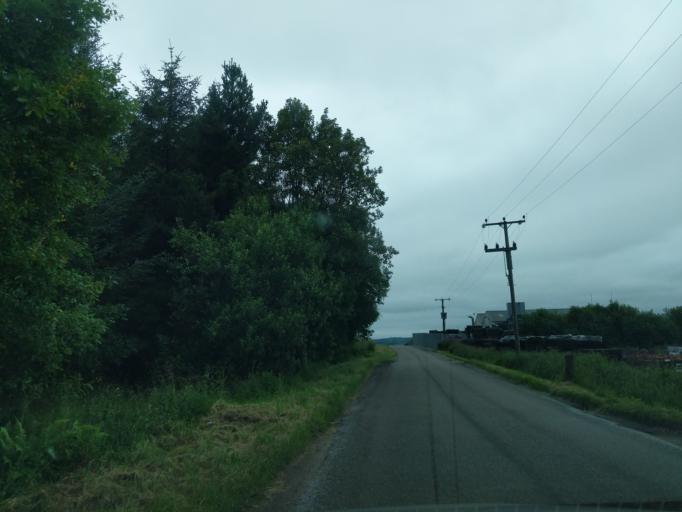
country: GB
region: Scotland
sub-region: Moray
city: Rothes
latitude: 57.4802
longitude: -3.1782
